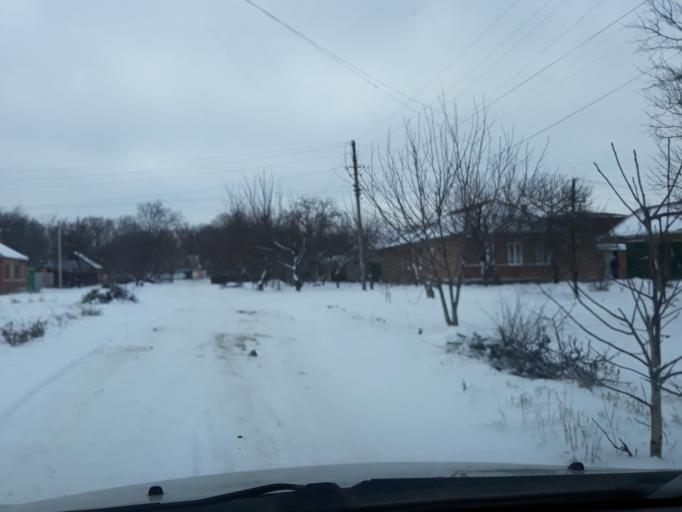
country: RU
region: Rostov
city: Taganrog
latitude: 47.2293
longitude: 38.8906
